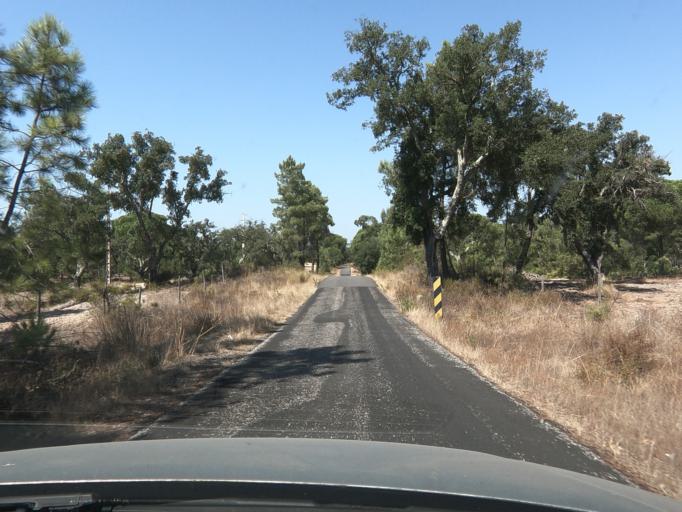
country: PT
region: Setubal
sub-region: Alcacer do Sal
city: Alcacer do Sal
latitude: 38.2643
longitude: -8.3133
